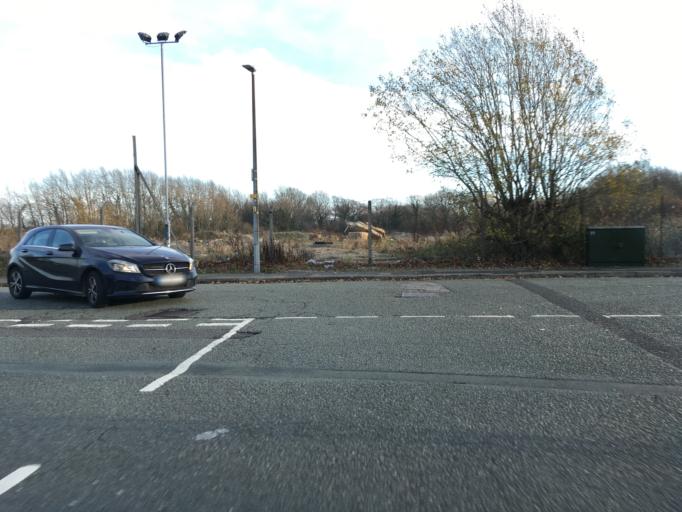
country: GB
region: England
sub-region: Borough of Stockport
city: Cheadle Hulme
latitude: 53.3525
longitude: -2.2053
